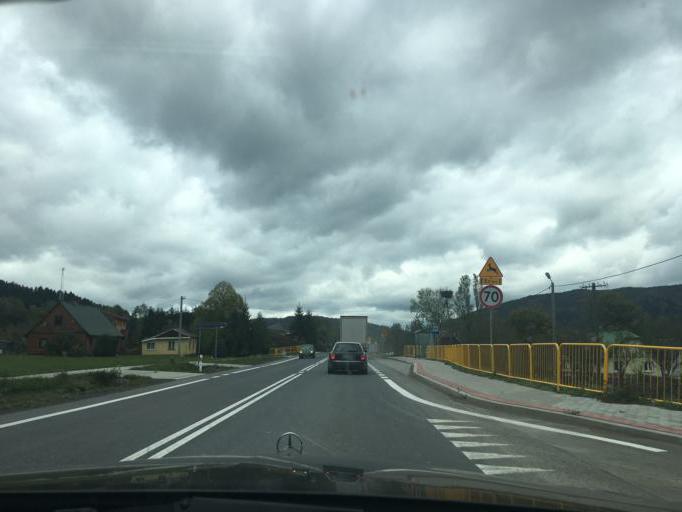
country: PL
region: Subcarpathian Voivodeship
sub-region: Powiat krosnienski
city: Dukla
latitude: 49.5008
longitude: 21.6995
